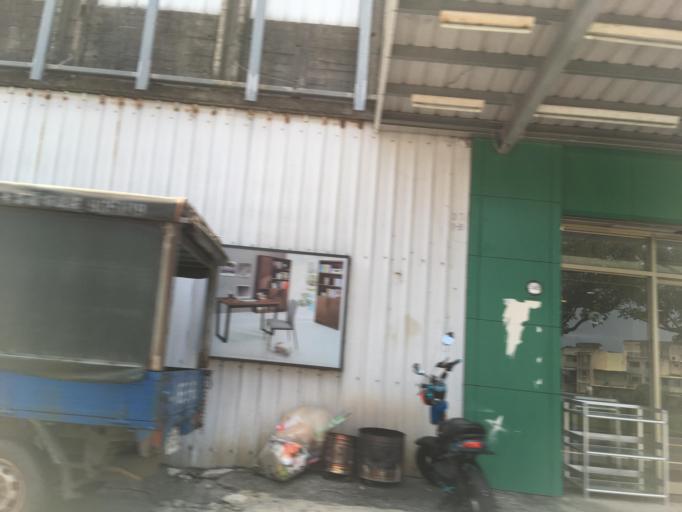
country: TW
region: Taiwan
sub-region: Yilan
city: Yilan
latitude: 24.6523
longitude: 121.7634
